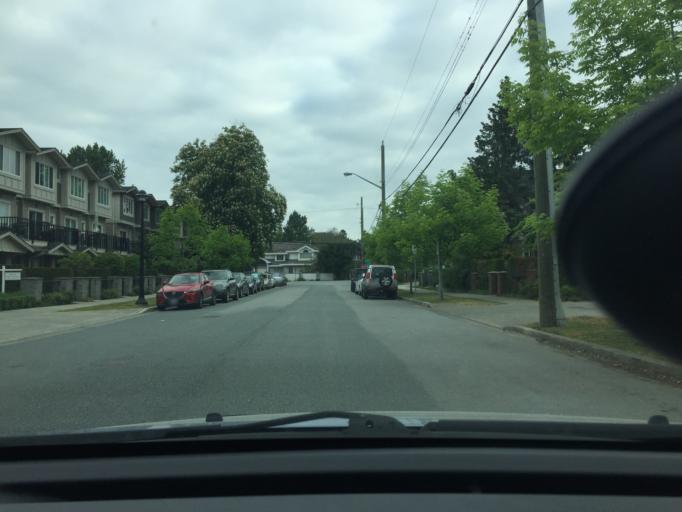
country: CA
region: British Columbia
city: Richmond
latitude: 49.1620
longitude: -123.1198
